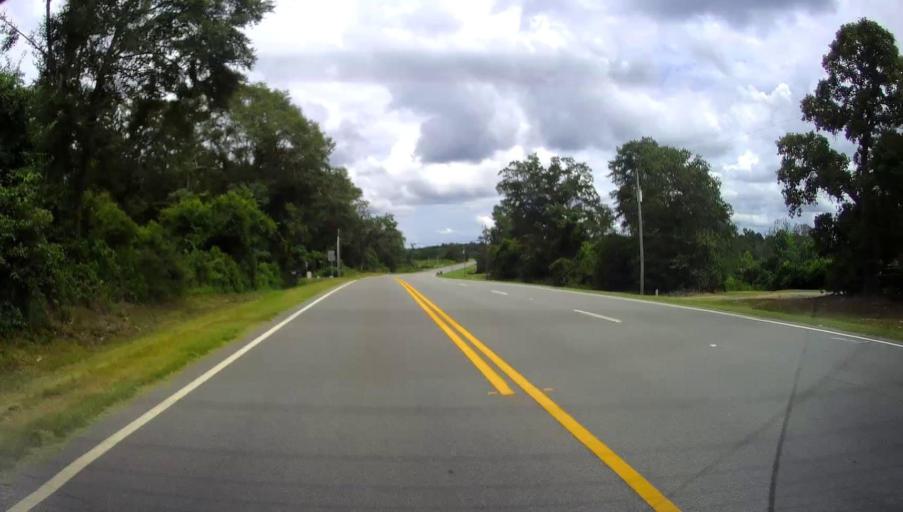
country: US
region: Georgia
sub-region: Macon County
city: Oglethorpe
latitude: 32.2821
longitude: -84.1477
